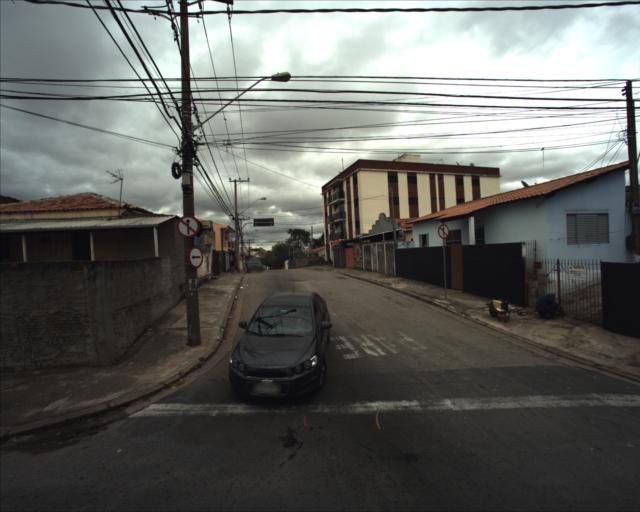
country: BR
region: Sao Paulo
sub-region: Sorocaba
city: Sorocaba
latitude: -23.4823
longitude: -47.4693
